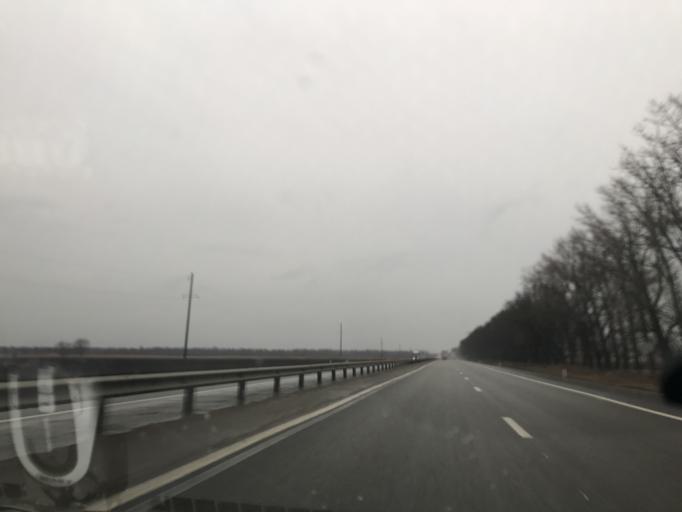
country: RU
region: Krasnodarskiy
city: Kislyakovskaya
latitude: 46.3832
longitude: 39.7438
